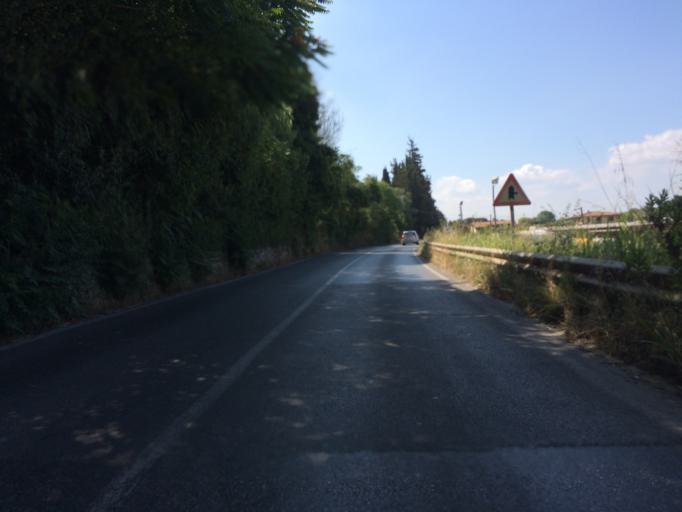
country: IT
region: Tuscany
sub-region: Provincia di Lucca
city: Piano di Conca
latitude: 43.8982
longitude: 10.2868
